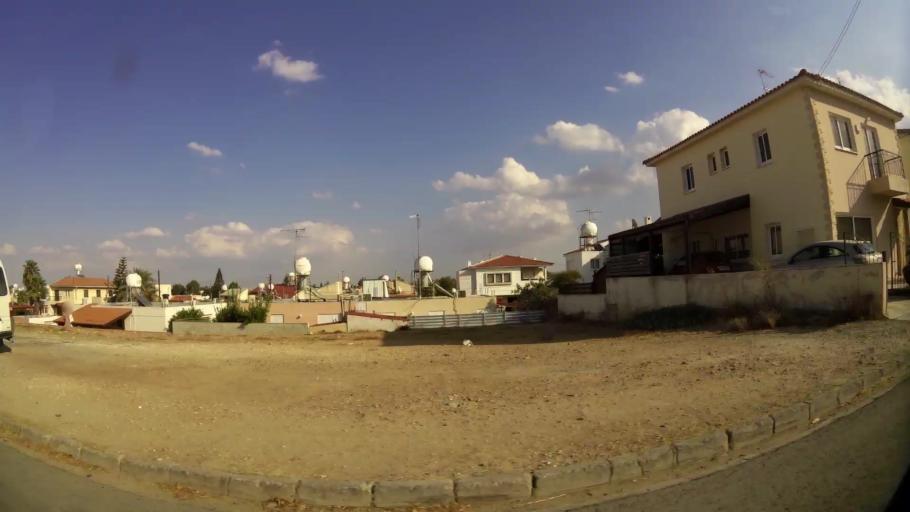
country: CY
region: Lefkosia
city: Kato Deftera
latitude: 35.1174
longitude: 33.2939
